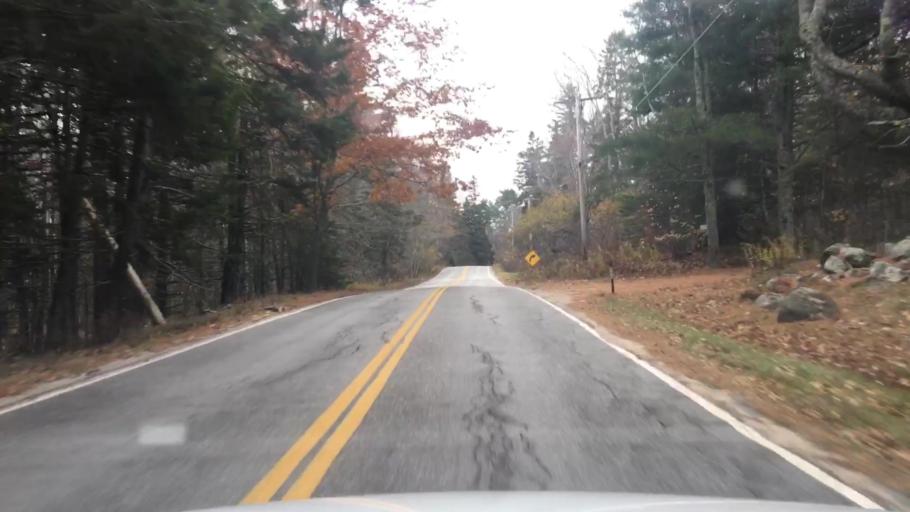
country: US
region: Maine
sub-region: Hancock County
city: Sedgwick
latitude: 44.2927
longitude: -68.5552
